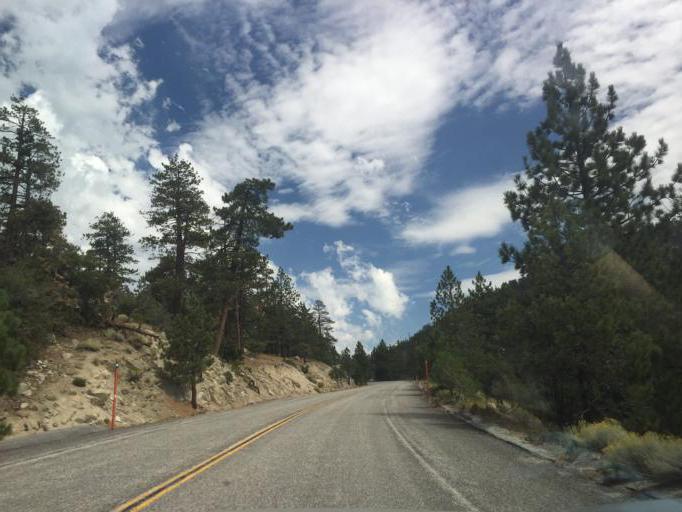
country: US
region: California
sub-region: Los Angeles County
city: Littlerock
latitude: 34.3530
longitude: -117.9432
